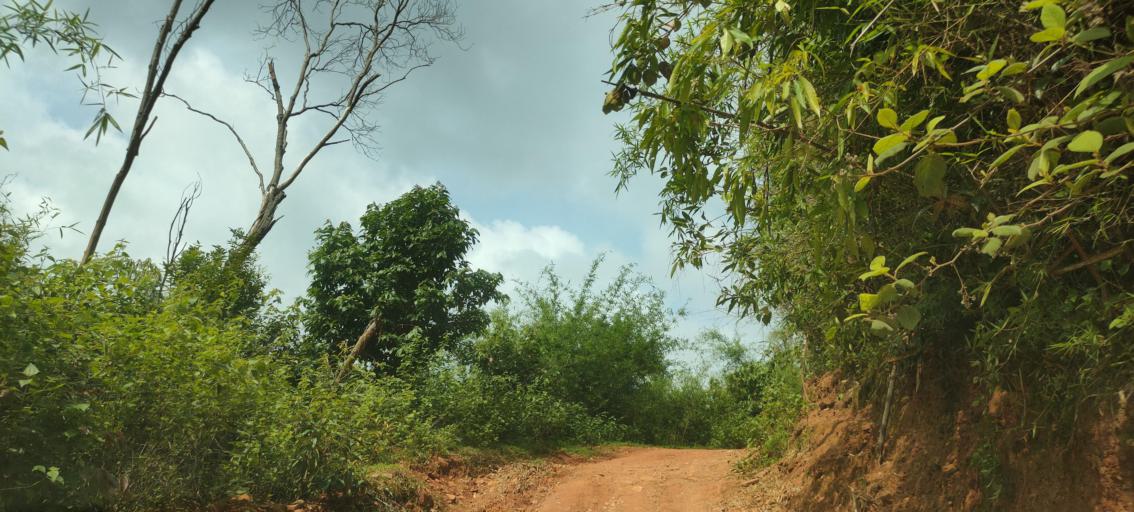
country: LA
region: Loungnamtha
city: Muang Nale
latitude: 20.4267
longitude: 101.4693
